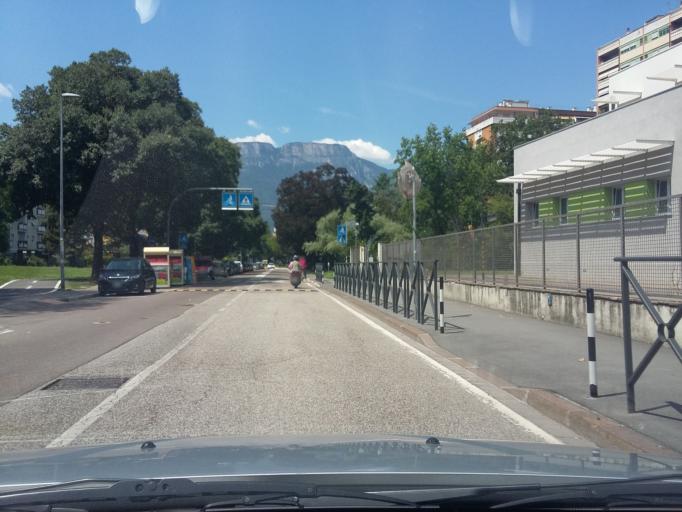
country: IT
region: Trentino-Alto Adige
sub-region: Bolzano
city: Bolzano
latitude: 46.4905
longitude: 11.3233
